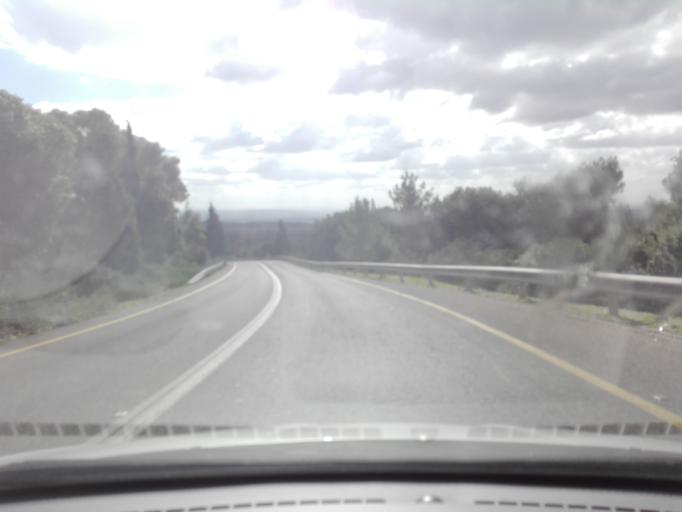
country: IL
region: Haifa
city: Daliyat el Karmil
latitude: 32.6731
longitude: 35.0547
